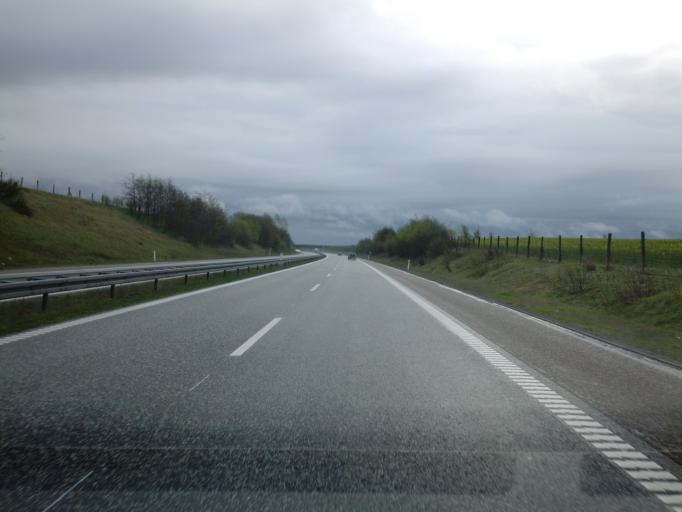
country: DK
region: North Denmark
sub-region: Bronderslev Kommune
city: Dronninglund
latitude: 57.2367
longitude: 10.2758
